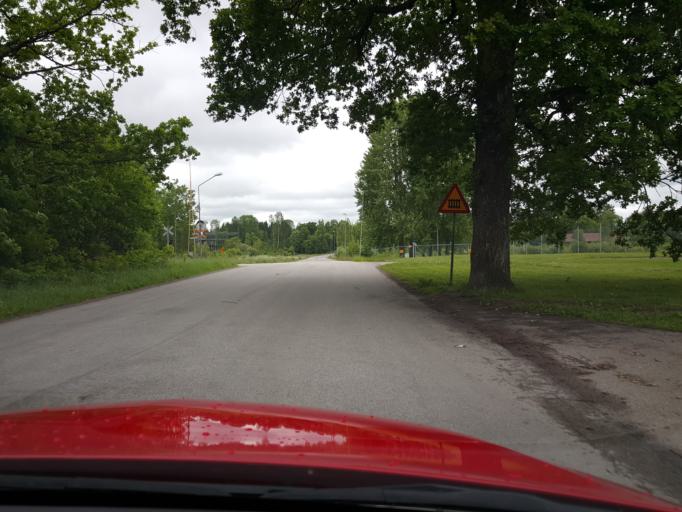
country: SE
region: Uppsala
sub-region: Osthammars Kommun
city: Gimo
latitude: 60.1752
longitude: 18.1777
